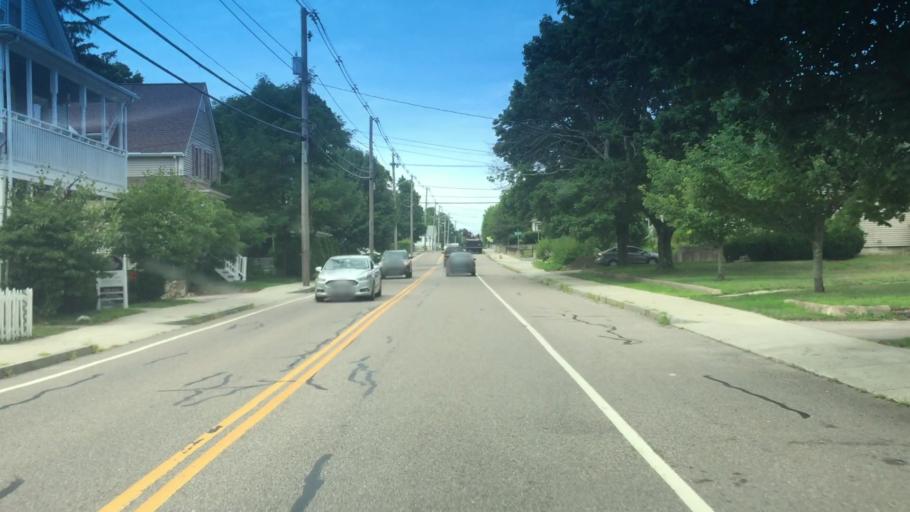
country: US
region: Massachusetts
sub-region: Norfolk County
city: Franklin
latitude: 42.0807
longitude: -71.4034
